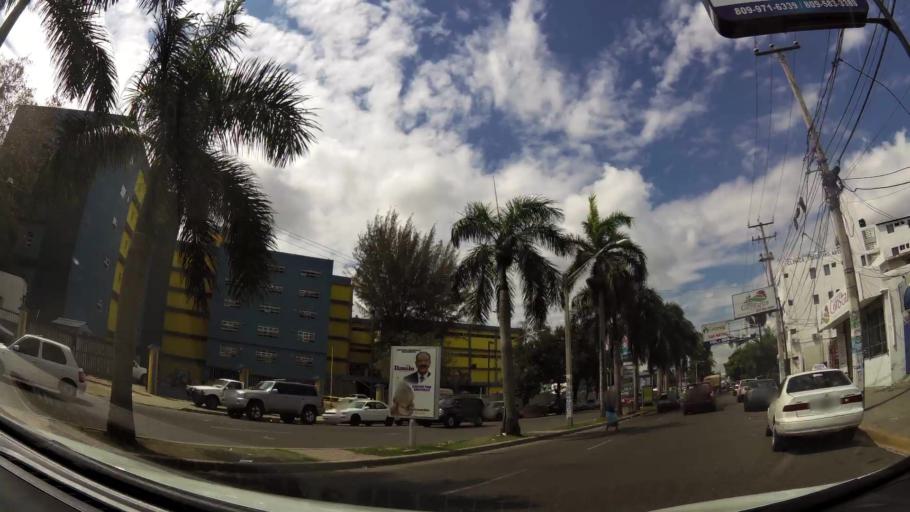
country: DO
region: Santiago
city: Santiago de los Caballeros
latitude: 19.4572
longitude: -70.6994
